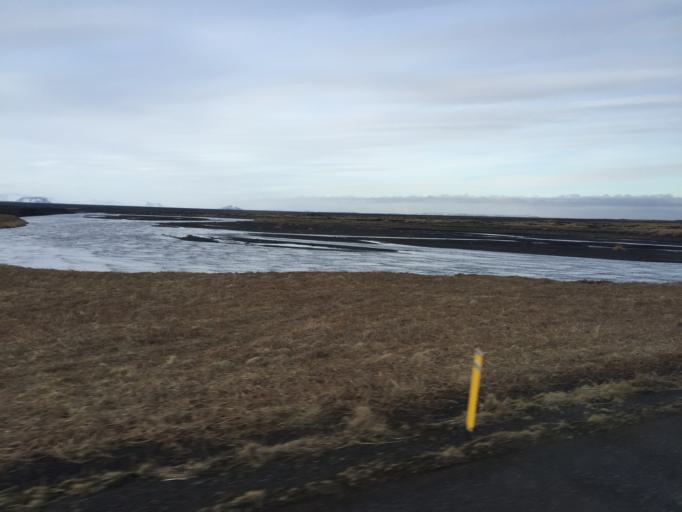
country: IS
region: South
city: Vestmannaeyjar
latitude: 63.4485
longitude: -18.6751
